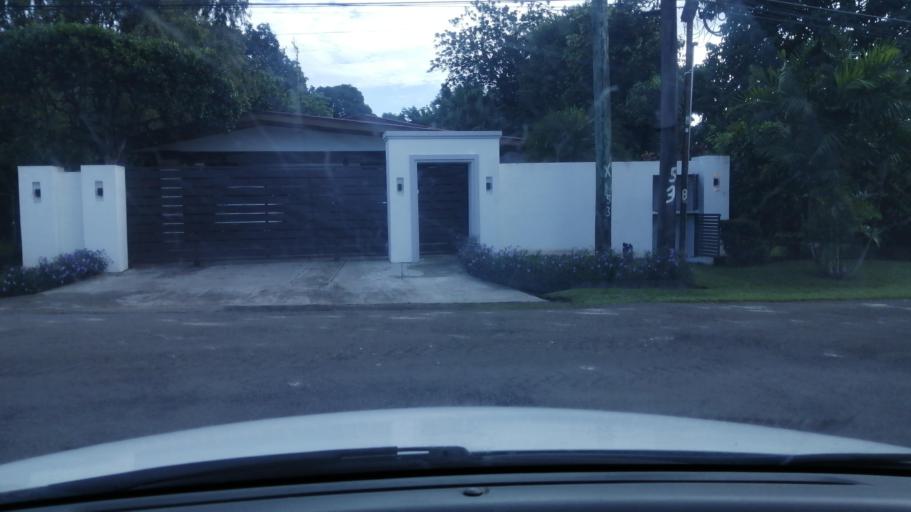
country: PA
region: Chiriqui
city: Mata del Nance
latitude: 8.4509
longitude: -82.4187
